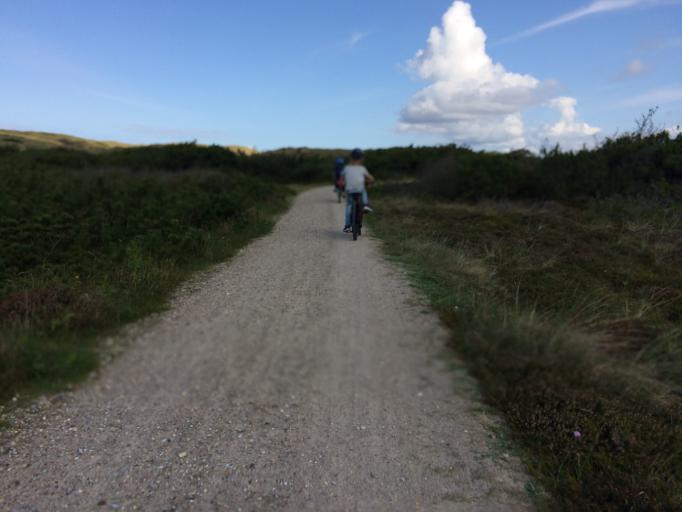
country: DK
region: Central Jutland
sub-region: Ringkobing-Skjern Kommune
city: Hvide Sande
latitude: 55.9438
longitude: 8.1490
